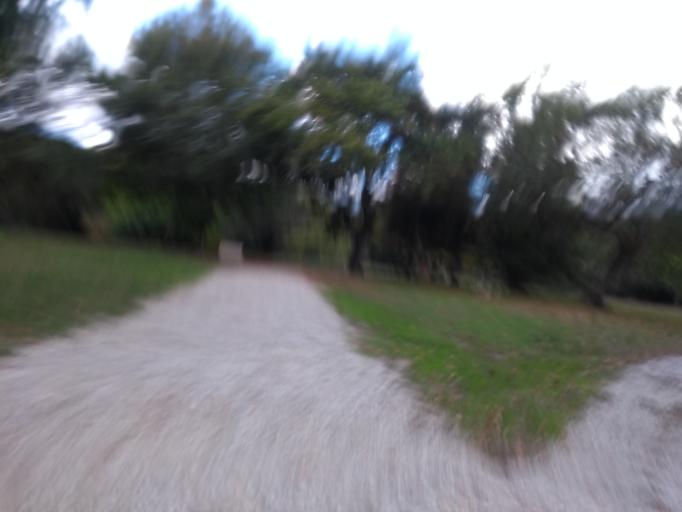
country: FR
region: Aquitaine
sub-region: Departement de la Gironde
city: Canejan
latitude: 44.7597
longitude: -0.6433
